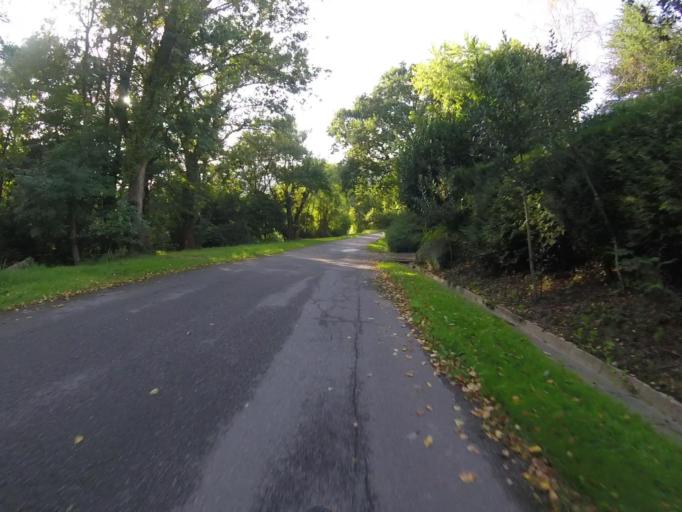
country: ES
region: Basque Country
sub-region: Provincia de Guipuzcoa
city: Irun
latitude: 43.3409
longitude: -1.8381
